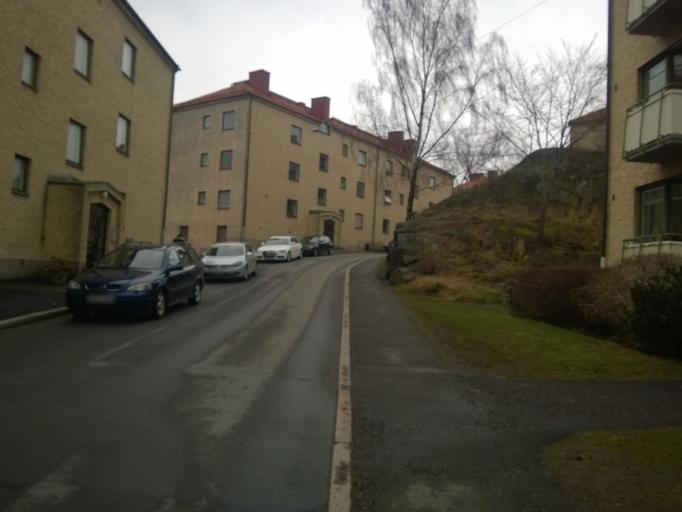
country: SE
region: Vaestra Goetaland
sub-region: Goteborg
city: Goeteborg
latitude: 57.6900
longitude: 11.9653
